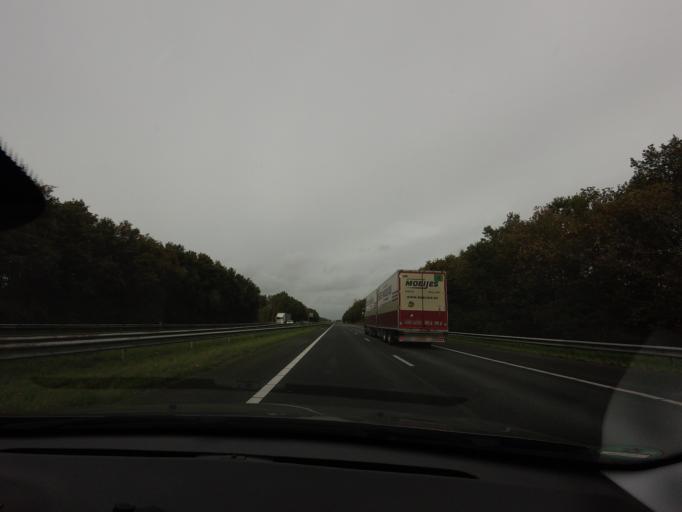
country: NL
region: Flevoland
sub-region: Gemeente Noordoostpolder
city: Emmeloord
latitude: 52.7068
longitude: 5.7725
